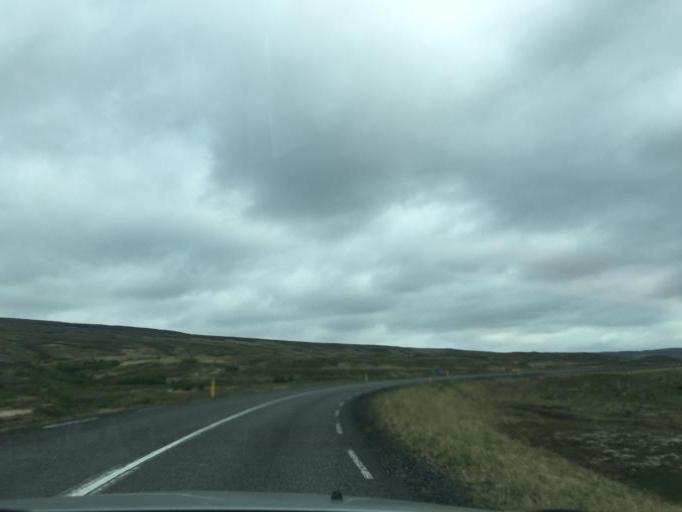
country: IS
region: South
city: Vestmannaeyjar
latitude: 64.2686
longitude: -20.1935
